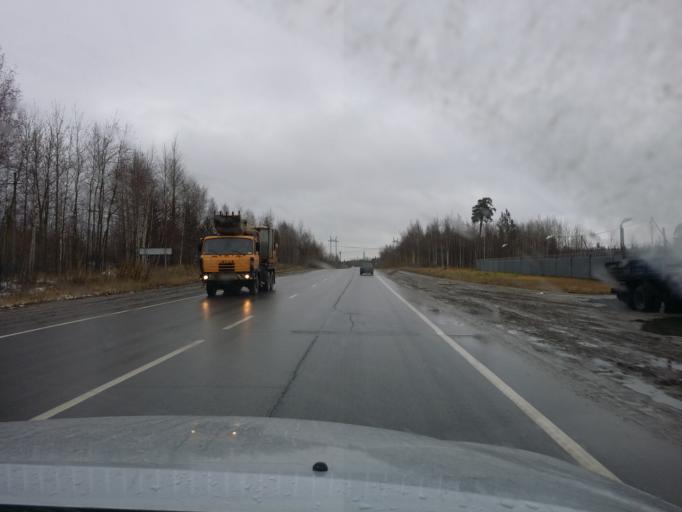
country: RU
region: Khanty-Mansiyskiy Avtonomnyy Okrug
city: Megion
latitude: 61.0760
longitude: 76.1170
